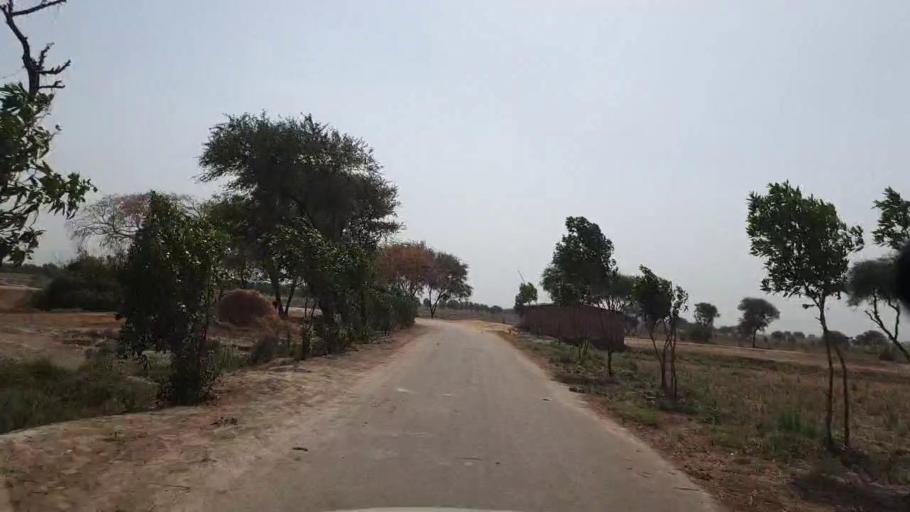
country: PK
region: Sindh
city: Matli
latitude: 25.0419
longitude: 68.6867
